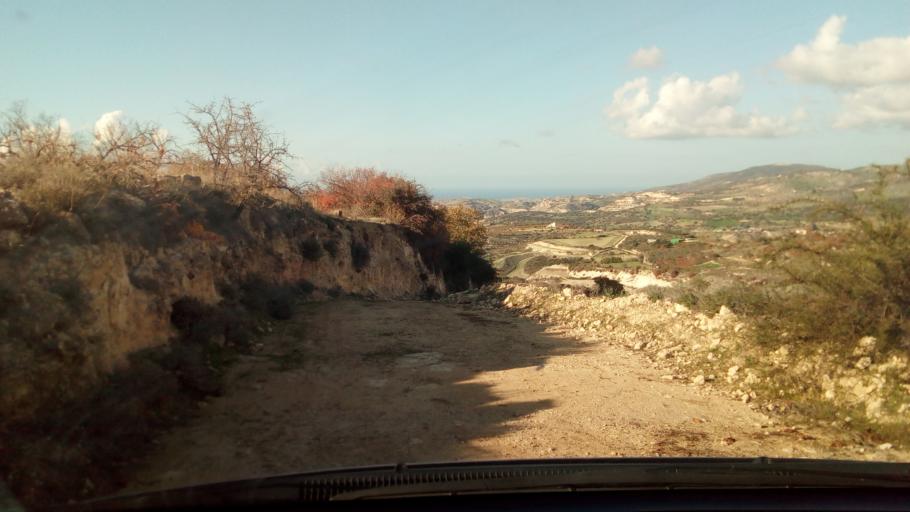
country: CY
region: Pafos
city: Polis
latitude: 34.9417
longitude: 32.4873
